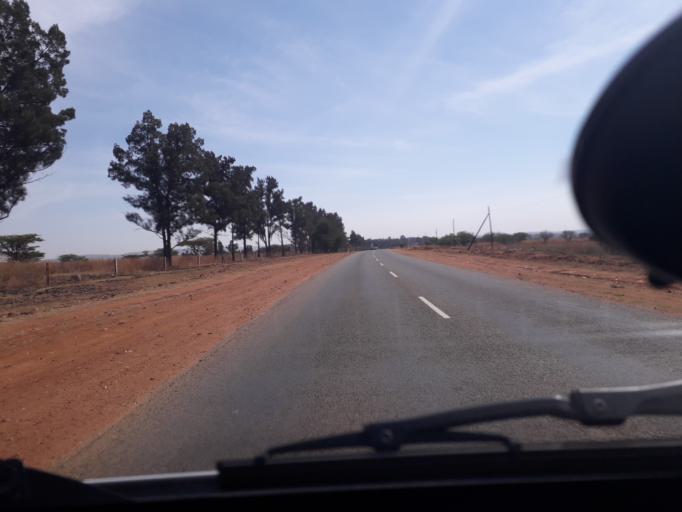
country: ZA
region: Gauteng
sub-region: West Rand District Municipality
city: Muldersdriseloop
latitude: -25.9981
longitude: 27.8574
